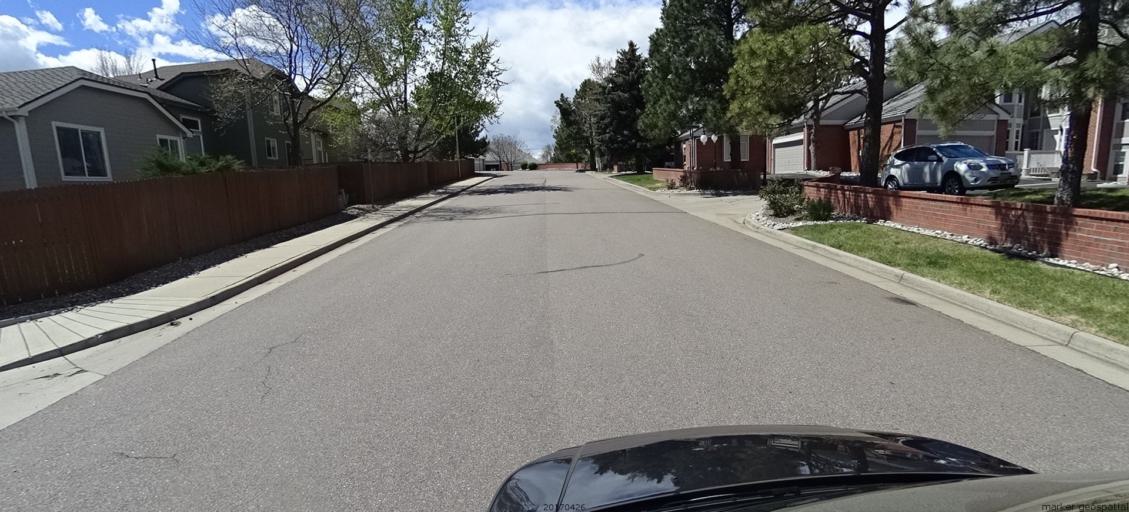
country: US
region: Colorado
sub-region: Adams County
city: Lone Tree
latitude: 39.5462
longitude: -104.8880
